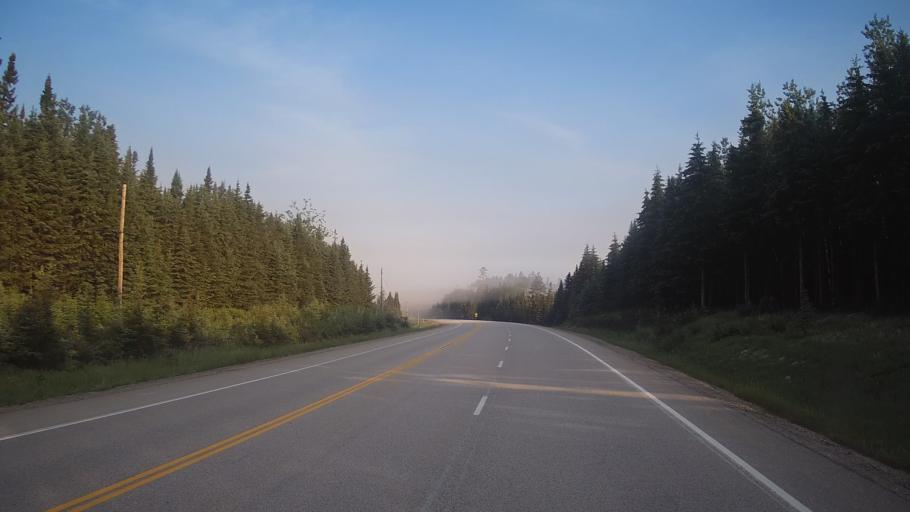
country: CA
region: Ontario
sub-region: Rainy River District
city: Atikokan
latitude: 49.2614
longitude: -91.2162
